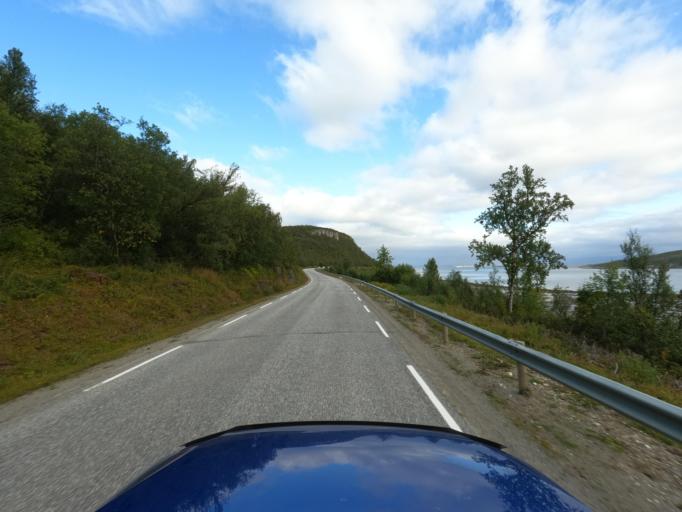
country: NO
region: Finnmark Fylke
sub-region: Porsanger
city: Lakselv
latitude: 70.2342
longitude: 24.9472
